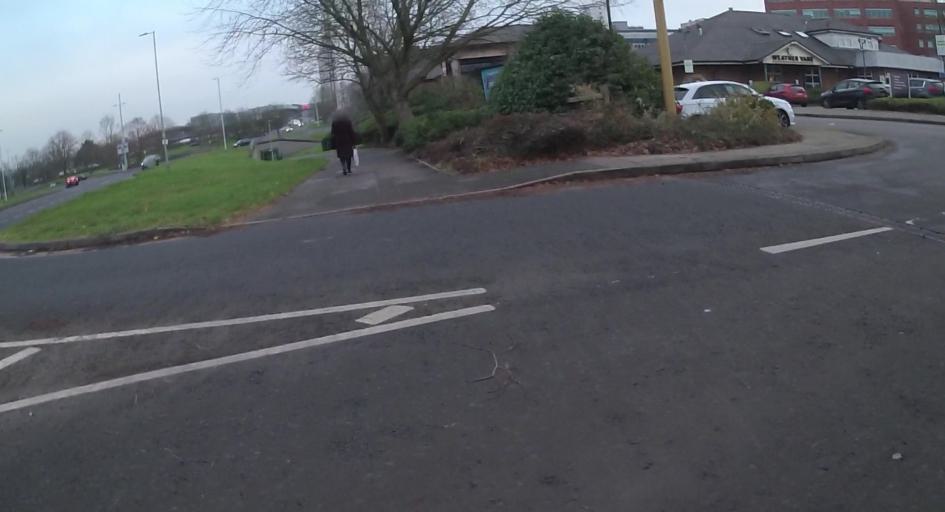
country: GB
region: England
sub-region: Bracknell Forest
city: Bracknell
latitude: 51.4179
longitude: -0.7570
